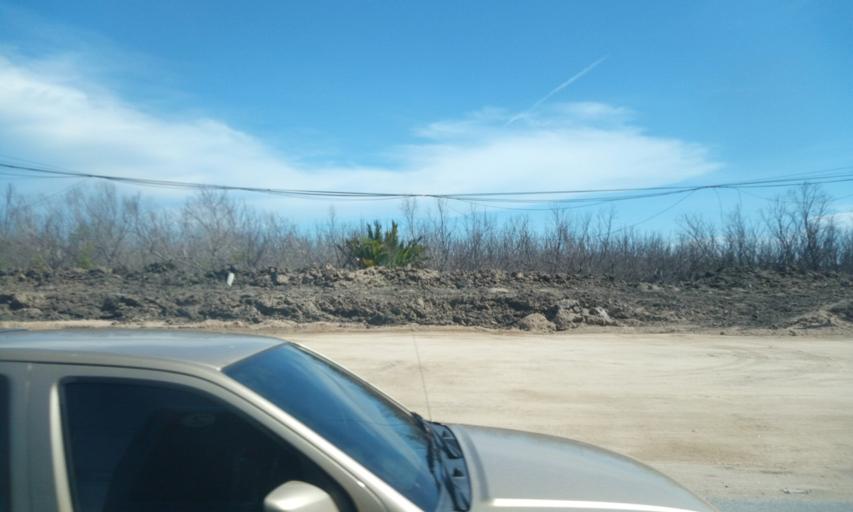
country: TH
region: Samut Prakan
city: Bang Bo District
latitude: 13.5025
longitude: 100.7599
